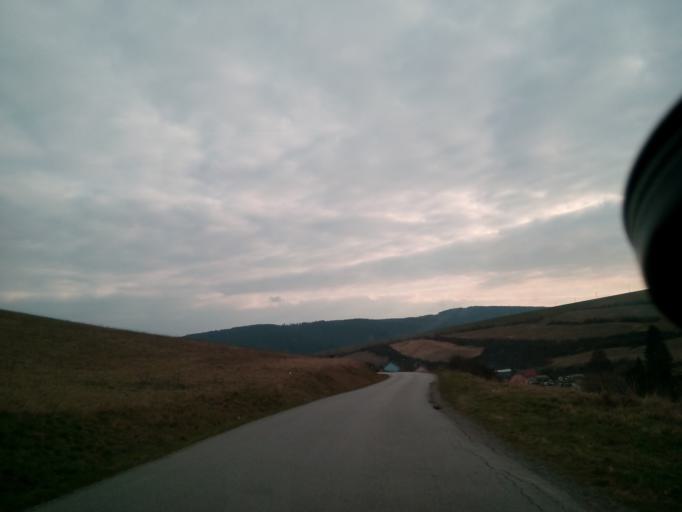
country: SK
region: Presovsky
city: Sabinov
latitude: 49.0410
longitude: 21.0193
